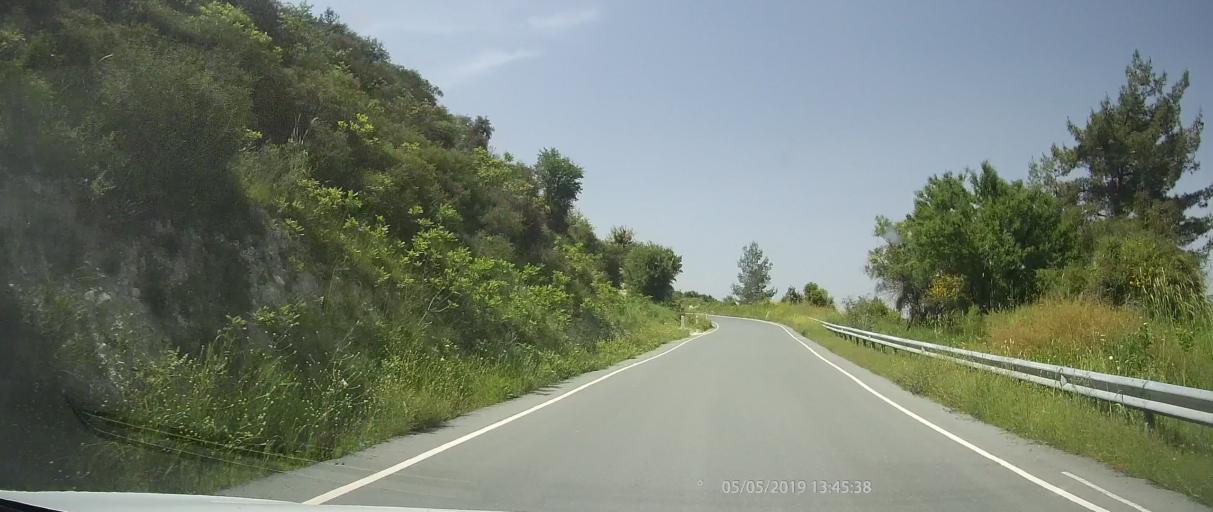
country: CY
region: Limassol
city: Pachna
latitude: 34.8705
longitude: 32.7801
